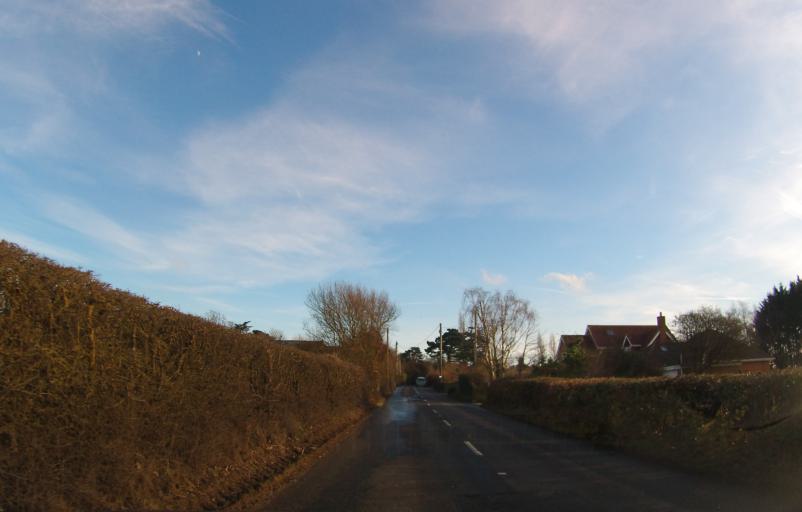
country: GB
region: England
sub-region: Isle of Wight
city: Newport
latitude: 50.7190
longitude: -1.2493
